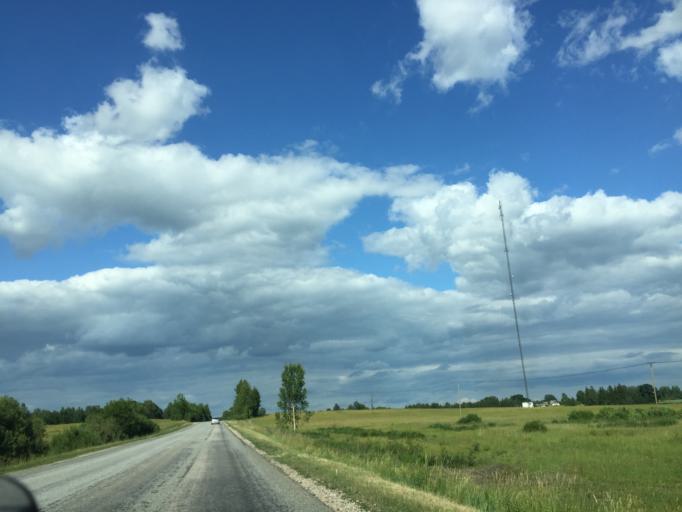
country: LV
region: Ogre
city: Jumprava
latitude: 56.7881
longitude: 25.0289
